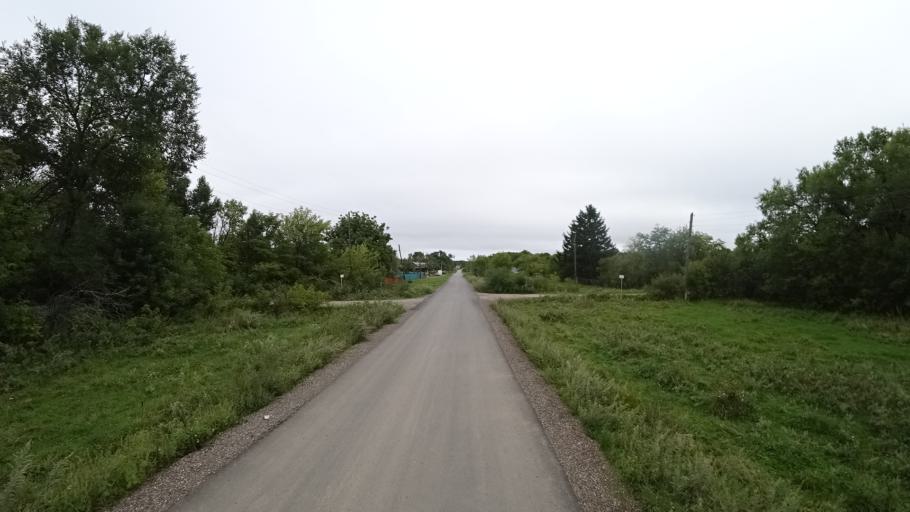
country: RU
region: Primorskiy
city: Monastyrishche
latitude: 44.0829
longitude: 132.5888
